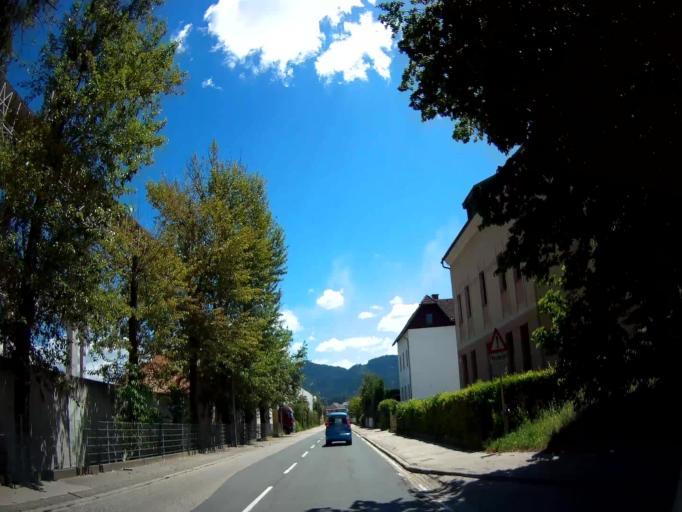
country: AT
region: Carinthia
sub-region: Politischer Bezirk Sankt Veit an der Glan
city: Sankt Veit an der Glan
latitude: 46.7593
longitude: 14.3743
